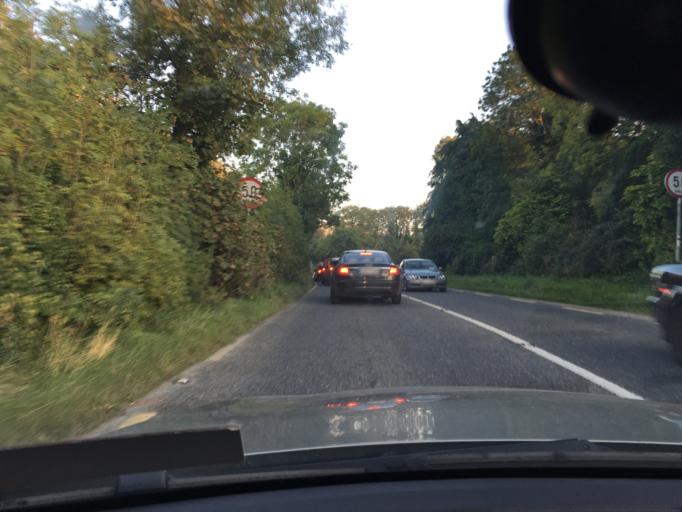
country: IE
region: Connaught
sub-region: County Galway
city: Gaillimh
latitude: 53.3007
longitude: -9.1030
